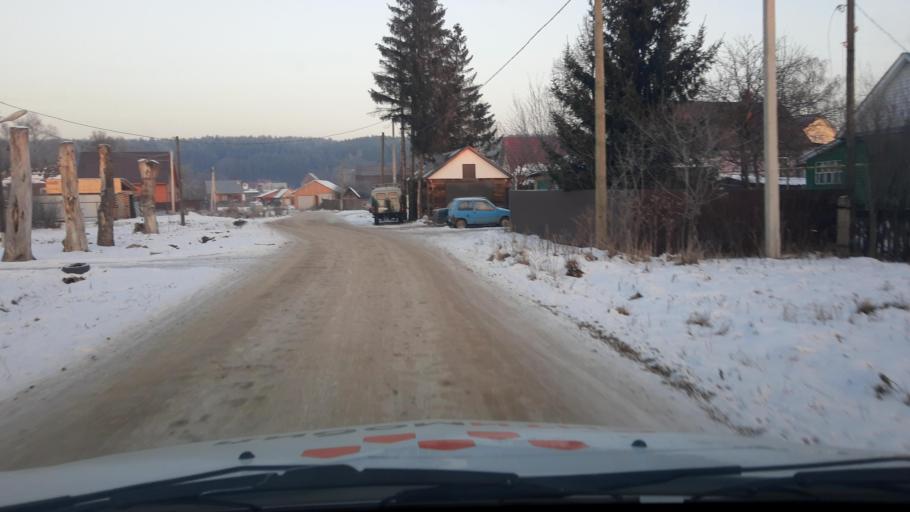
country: RU
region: Bashkortostan
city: Iglino
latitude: 54.8344
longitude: 56.4042
